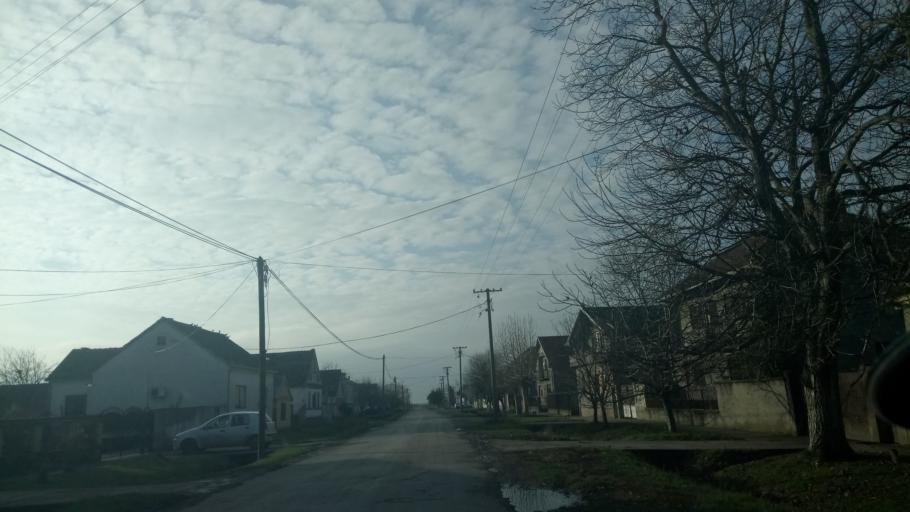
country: RS
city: Vojka
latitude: 44.9367
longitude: 20.1335
